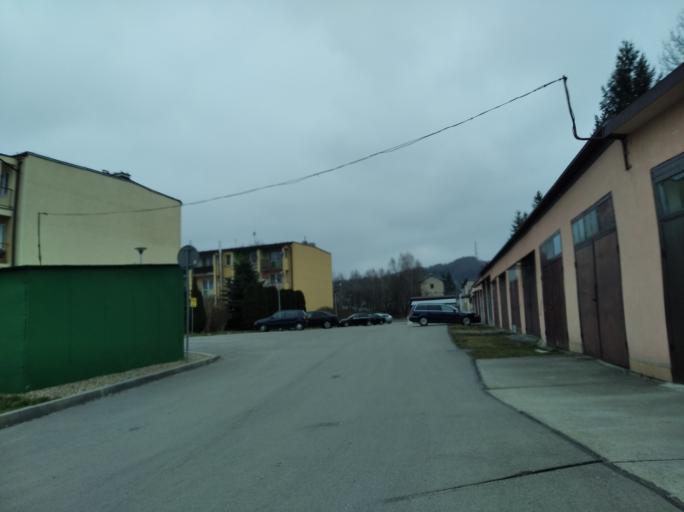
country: PL
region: Subcarpathian Voivodeship
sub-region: Powiat strzyzowski
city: Strzyzow
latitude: 49.8680
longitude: 21.7995
